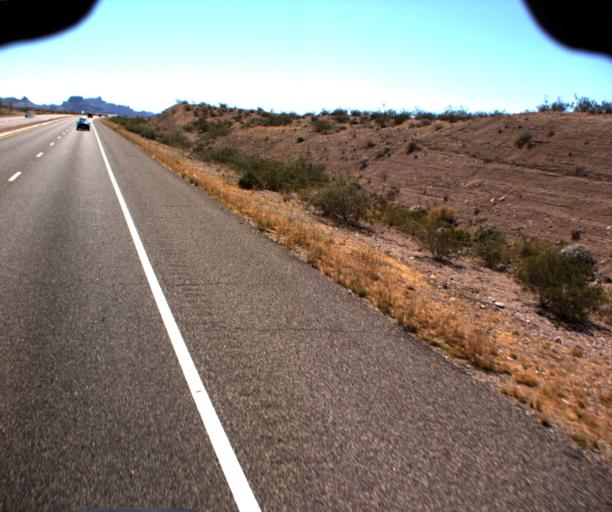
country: US
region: Nevada
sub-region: Clark County
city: Laughlin
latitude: 35.1891
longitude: -114.5111
